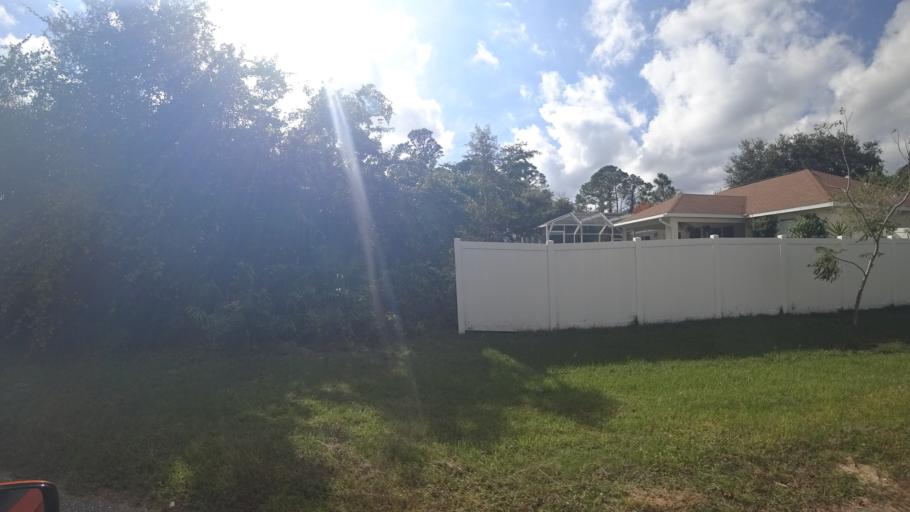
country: US
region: Florida
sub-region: Charlotte County
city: Port Charlotte
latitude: 27.0420
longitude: -82.1355
